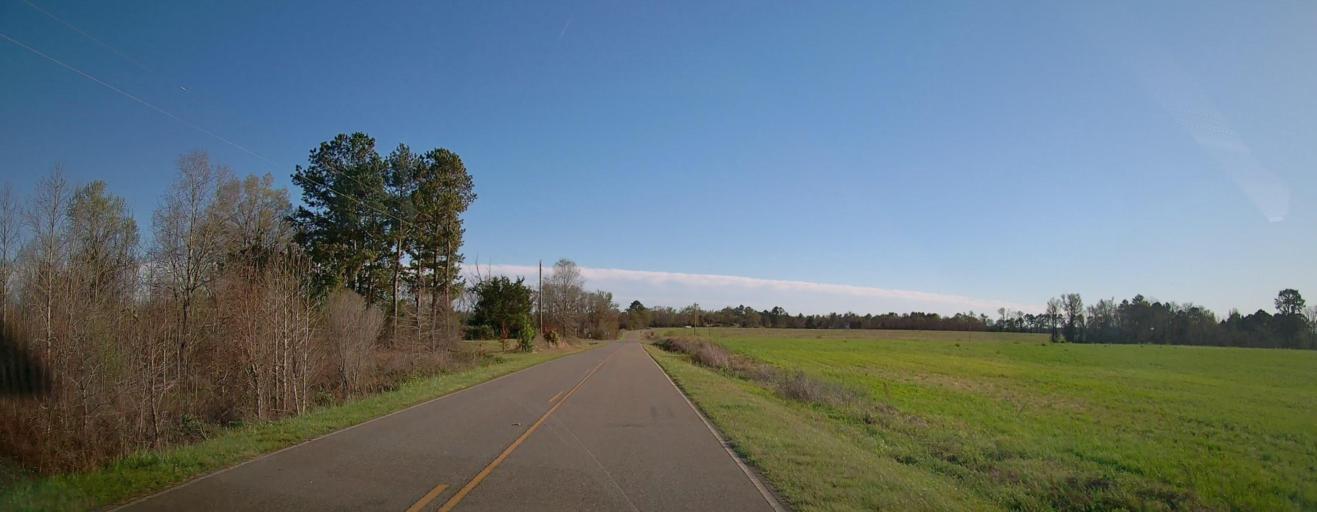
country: US
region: Georgia
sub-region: Pulaski County
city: Hawkinsville
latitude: 32.2482
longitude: -83.5879
